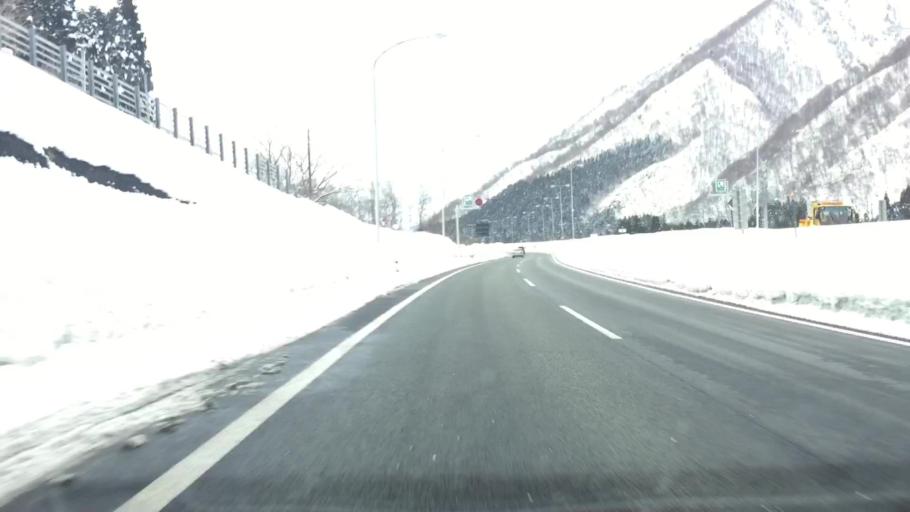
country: JP
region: Niigata
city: Shiozawa
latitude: 36.8711
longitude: 138.8650
